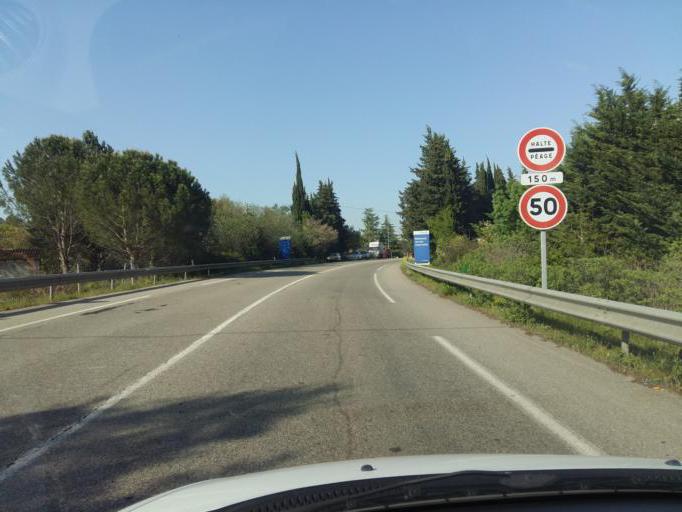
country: FR
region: Provence-Alpes-Cote d'Azur
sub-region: Departement du Var
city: Brignoles
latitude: 43.4177
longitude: 6.0632
